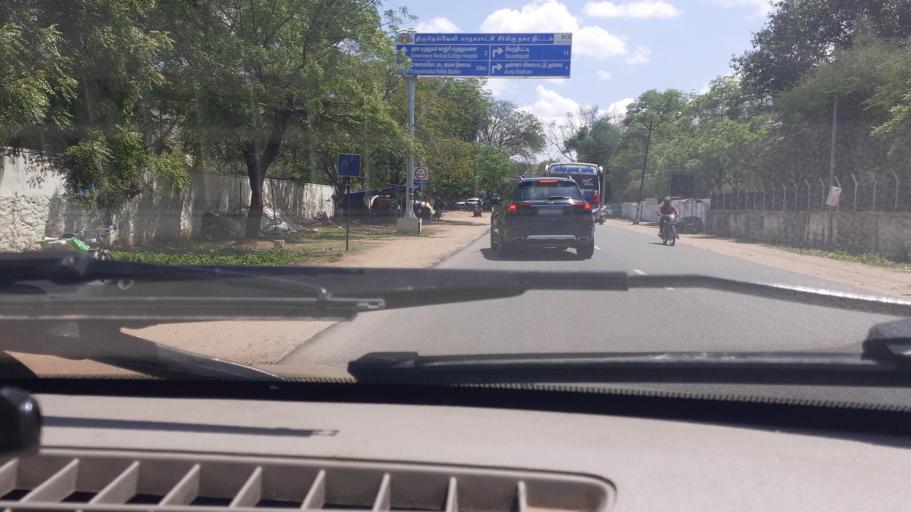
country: IN
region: Tamil Nadu
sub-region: Tirunelveli Kattabo
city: Tirunelveli
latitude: 8.7186
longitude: 77.7353
